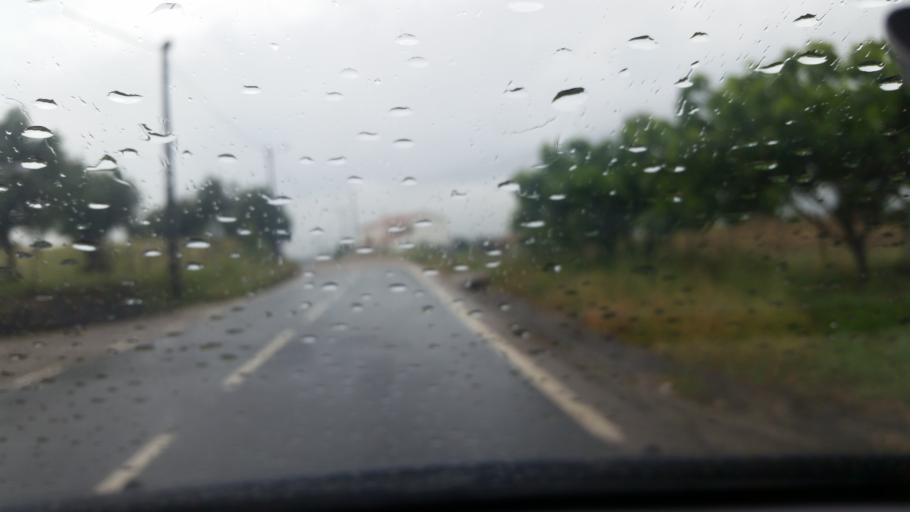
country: PT
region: Portalegre
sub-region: Ponte de Sor
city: Ponte de Sor
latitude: 39.1543
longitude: -7.9970
